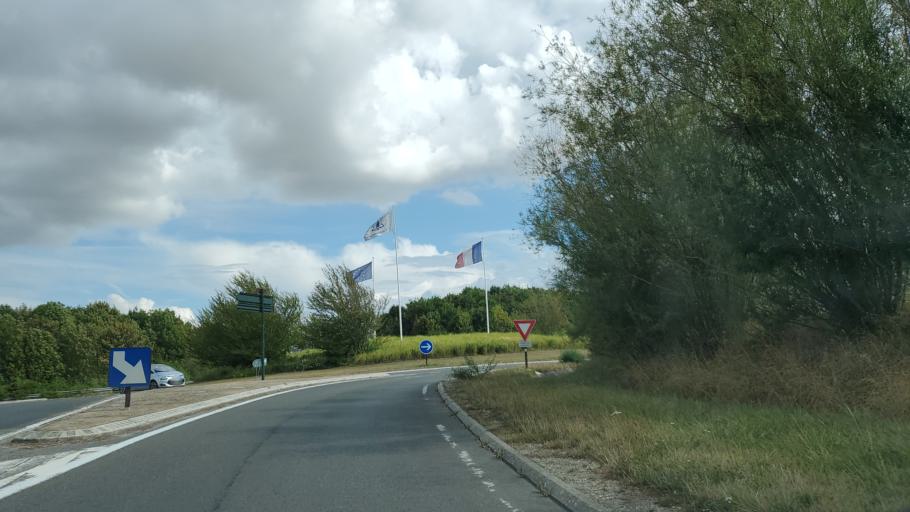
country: FR
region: Ile-de-France
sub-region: Departement de Seine-et-Marne
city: Coulommiers
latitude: 48.7980
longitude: 3.0942
